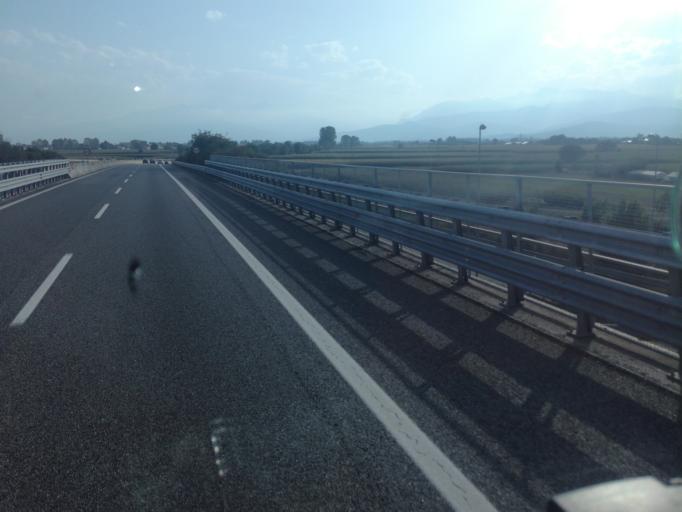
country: IT
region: Piedmont
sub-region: Provincia di Torino
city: Piscina
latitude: 44.9152
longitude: 7.4468
